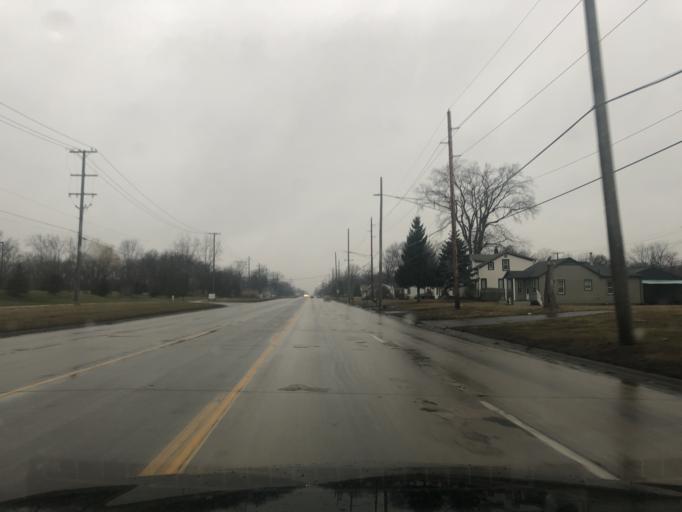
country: US
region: Michigan
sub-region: Wayne County
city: Inkster
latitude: 42.2681
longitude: -83.3147
